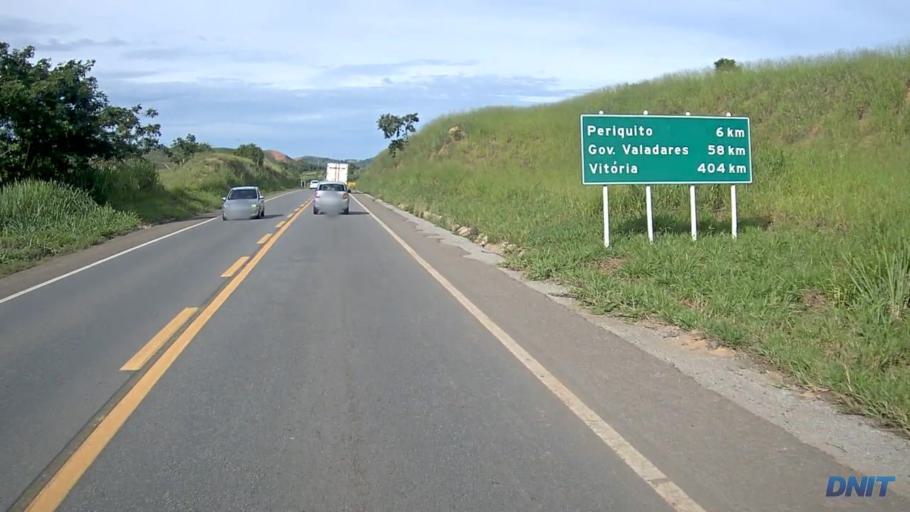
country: BR
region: Minas Gerais
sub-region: Belo Oriente
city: Belo Oriente
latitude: -19.1944
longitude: -42.2791
